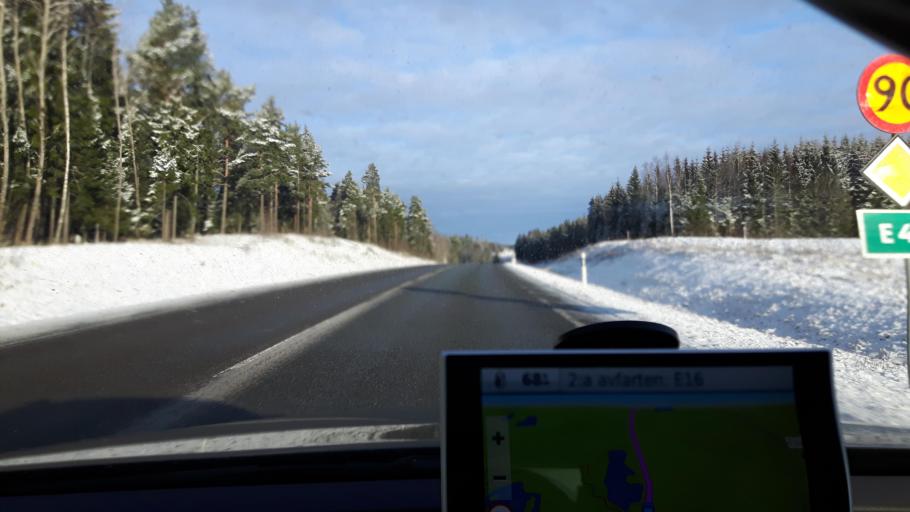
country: SE
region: Vaermland
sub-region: Karlstads Kommun
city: Edsvalla
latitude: 59.5568
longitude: 13.1886
